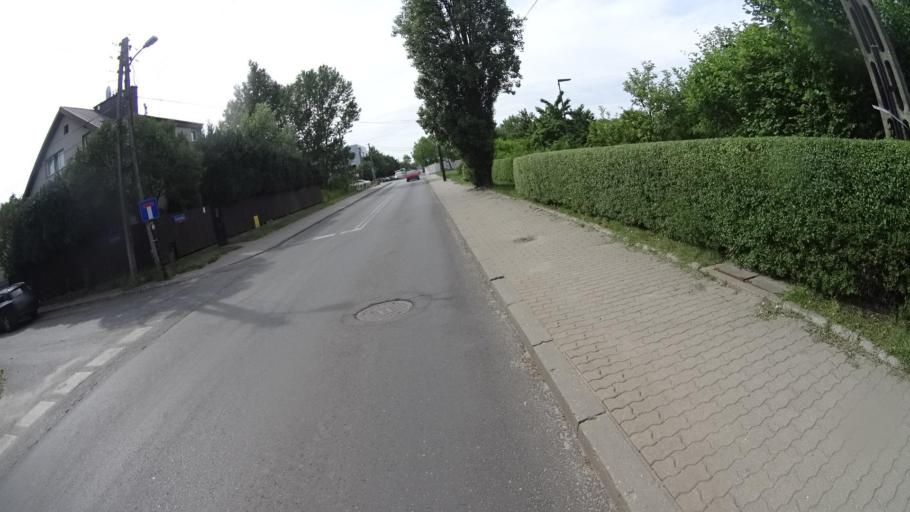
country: PL
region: Masovian Voivodeship
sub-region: Warszawa
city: Wlochy
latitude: 52.1879
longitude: 20.9451
